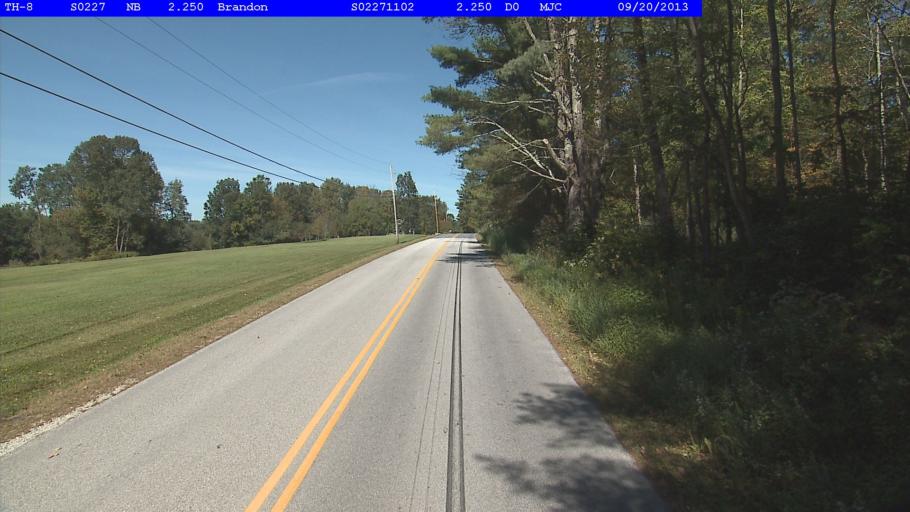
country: US
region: Vermont
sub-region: Rutland County
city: Brandon
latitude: 43.8068
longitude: -73.0564
